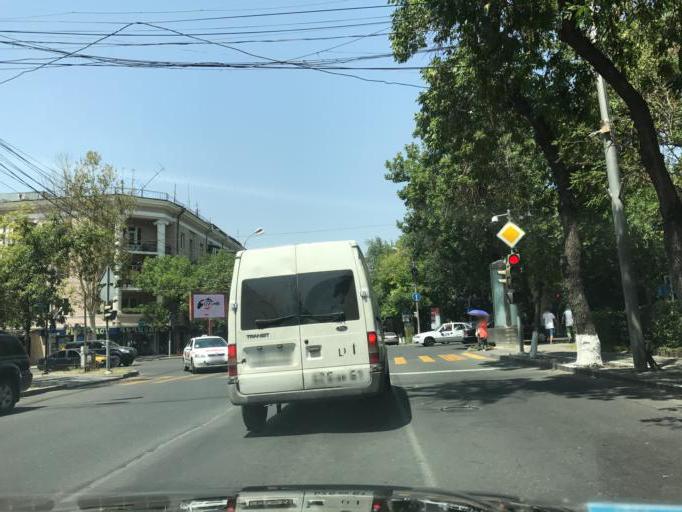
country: AM
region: Yerevan
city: Yerevan
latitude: 40.1870
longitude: 44.5203
